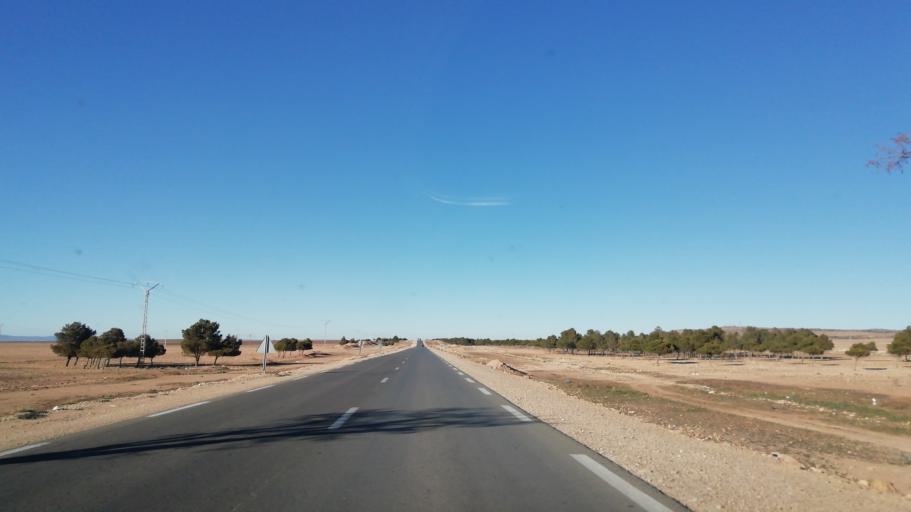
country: DZ
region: Tlemcen
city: Sebdou
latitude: 34.2353
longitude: -1.2565
